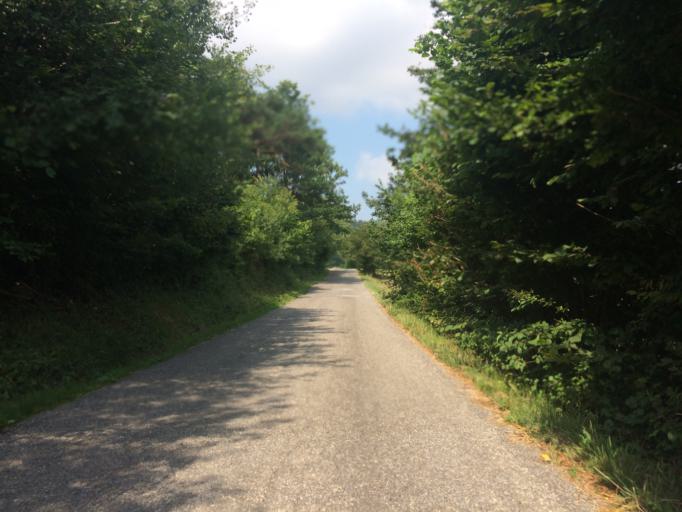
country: IT
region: Liguria
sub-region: Provincia di Savona
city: Giusvalla
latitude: 44.4629
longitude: 8.3536
